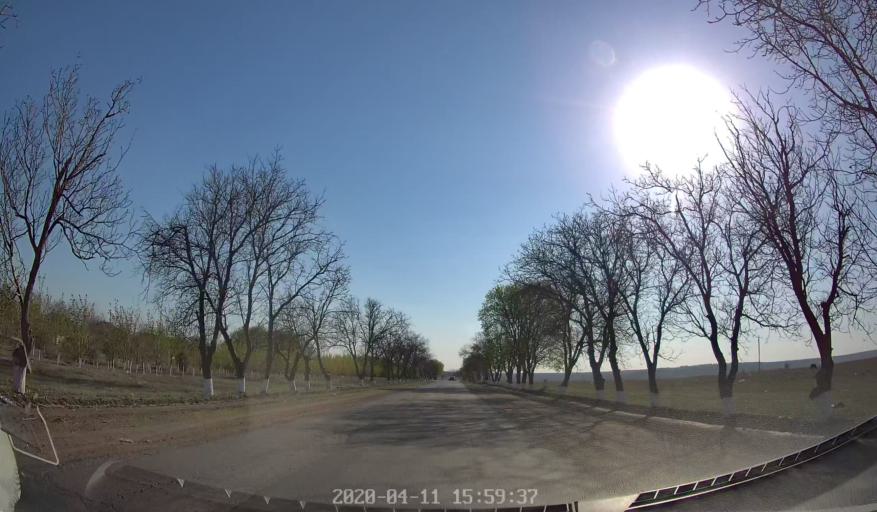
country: MD
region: Chisinau
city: Vadul lui Voda
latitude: 47.0810
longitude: 29.1399
